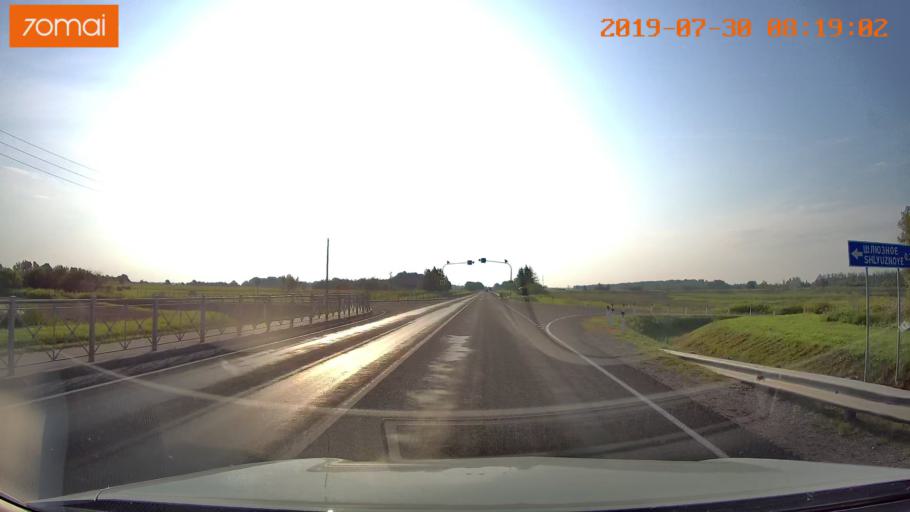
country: RU
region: Kaliningrad
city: Zheleznodorozhnyy
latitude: 54.6301
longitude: 21.4802
